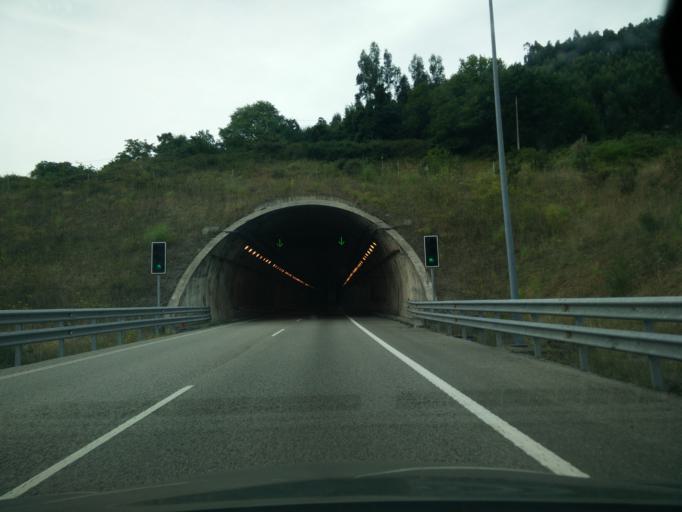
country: ES
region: Asturias
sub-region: Province of Asturias
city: Arriba
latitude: 43.4820
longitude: -5.5279
